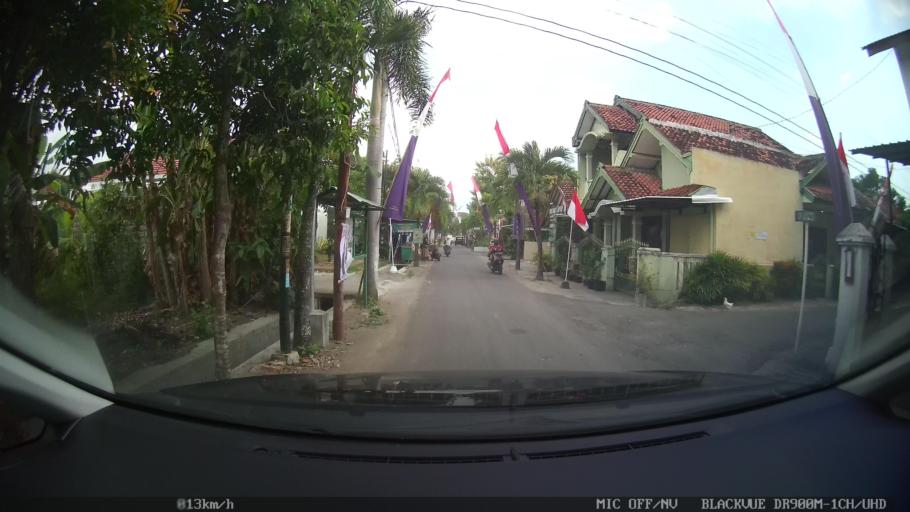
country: ID
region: Daerah Istimewa Yogyakarta
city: Yogyakarta
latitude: -7.8203
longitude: 110.4040
